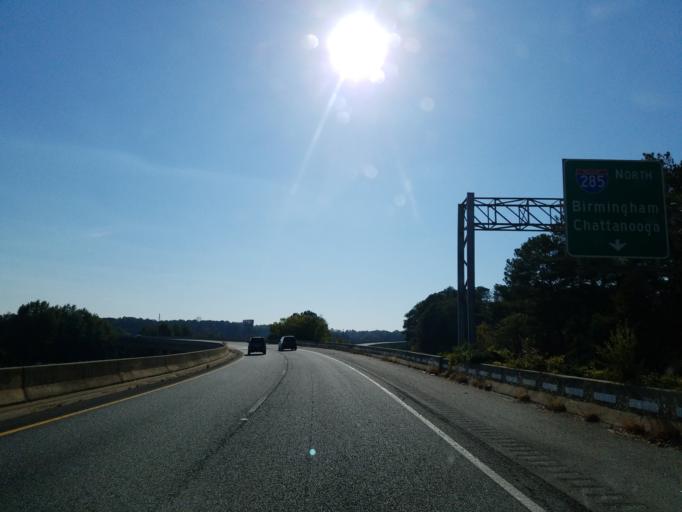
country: US
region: Georgia
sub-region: Fulton County
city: College Park
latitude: 33.6233
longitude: -84.4592
